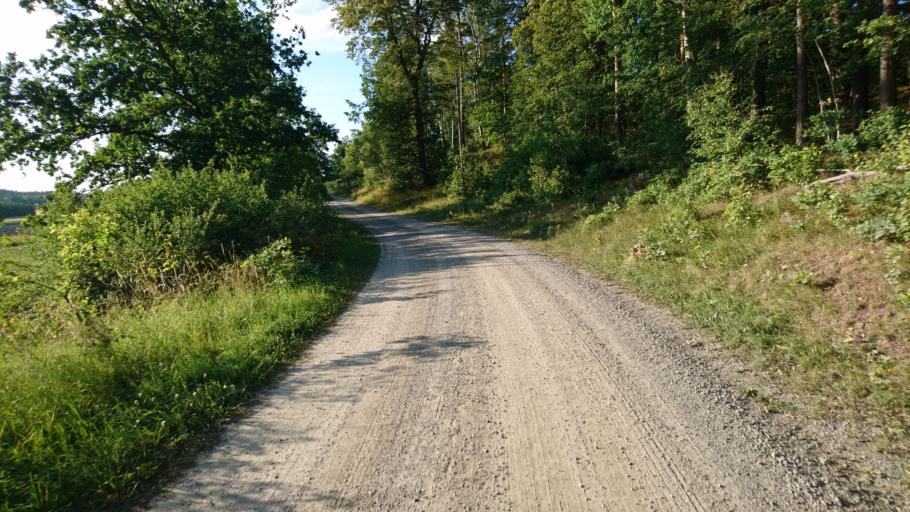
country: SE
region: Soedermanland
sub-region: Strangnas Kommun
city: Stallarholmen
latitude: 59.3862
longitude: 17.3083
